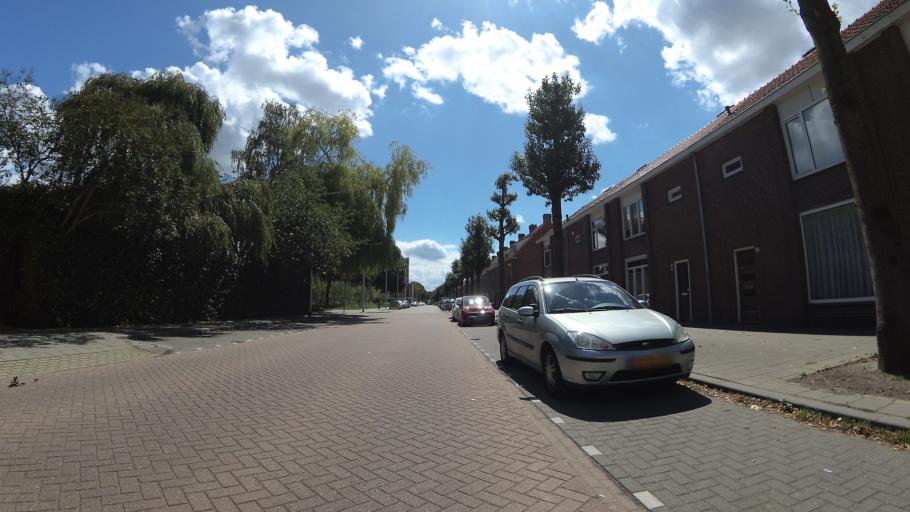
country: NL
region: North Brabant
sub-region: Gemeente Goirle
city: Goirle
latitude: 51.5531
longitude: 5.0524
